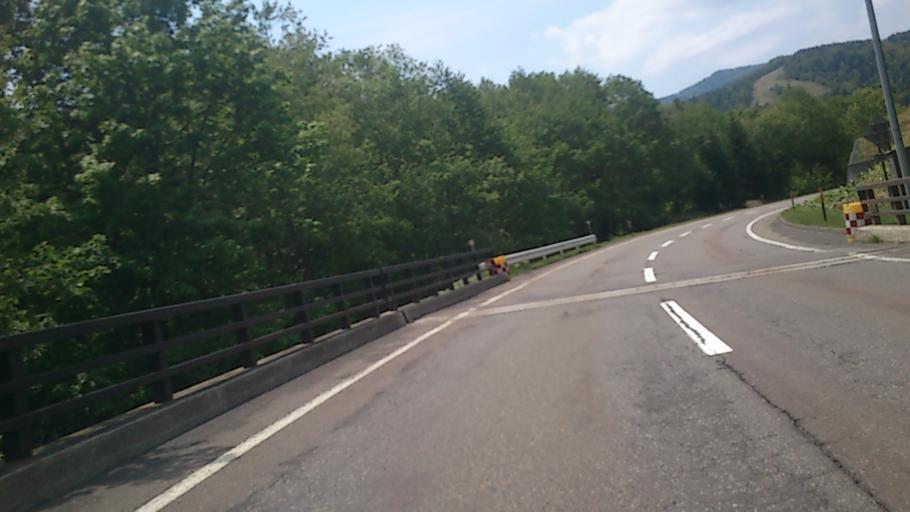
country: JP
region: Hokkaido
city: Otofuke
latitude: 43.3721
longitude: 143.1999
